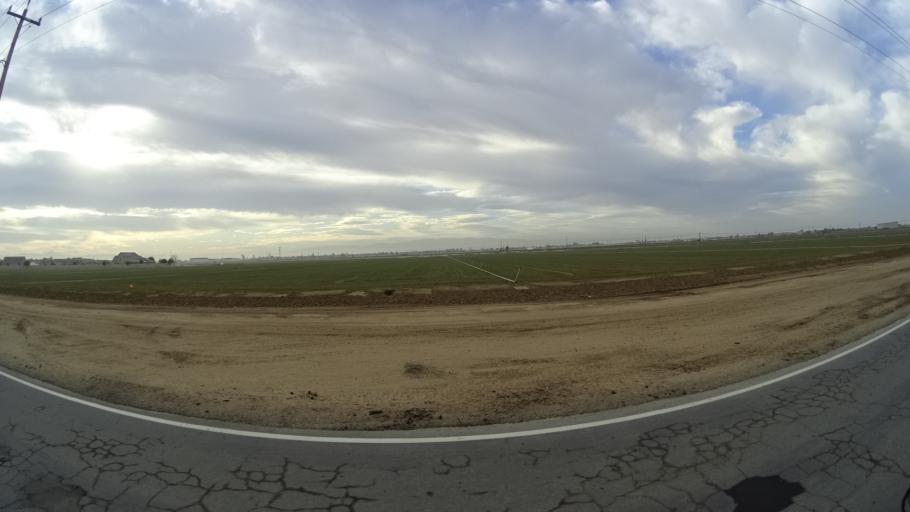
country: US
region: California
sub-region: Kern County
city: Rosedale
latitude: 35.4121
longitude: -119.1571
